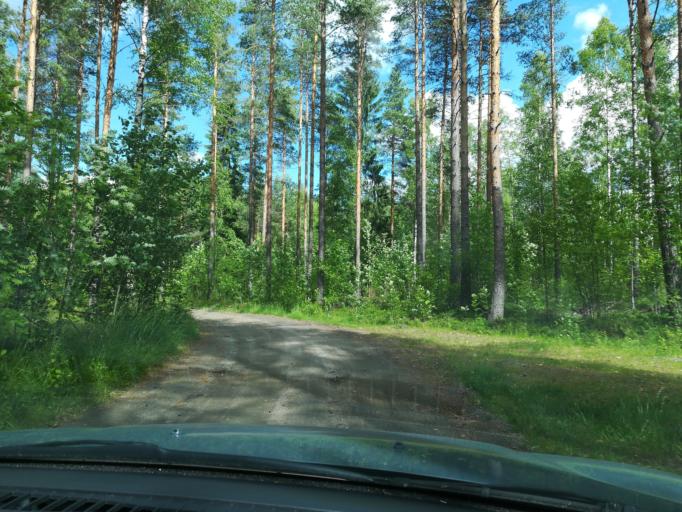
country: FI
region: Southern Savonia
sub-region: Mikkeli
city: Hirvensalmi
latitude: 61.6502
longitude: 26.7779
